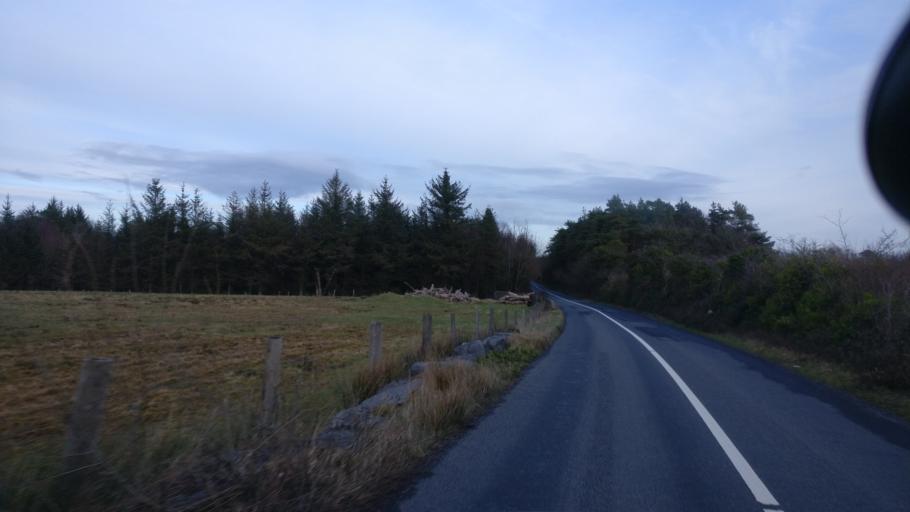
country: IE
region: Connaught
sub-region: County Galway
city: Oughterard
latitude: 53.5312
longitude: -9.3335
